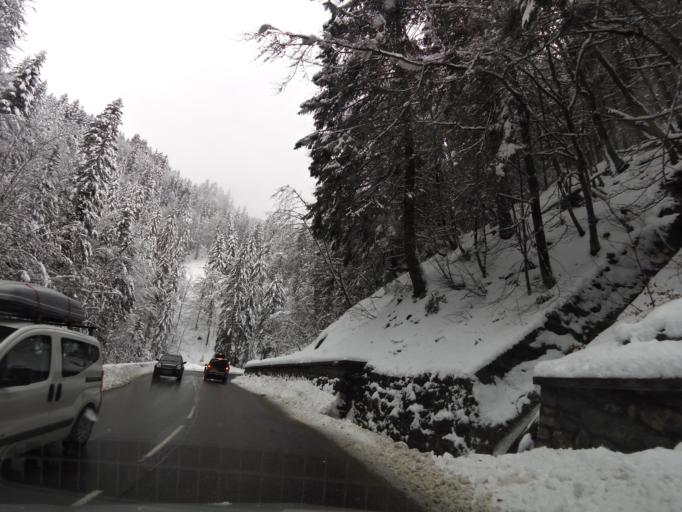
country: FR
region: Rhone-Alpes
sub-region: Departement de la Haute-Savoie
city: Les Gets
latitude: 46.1415
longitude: 6.6406
